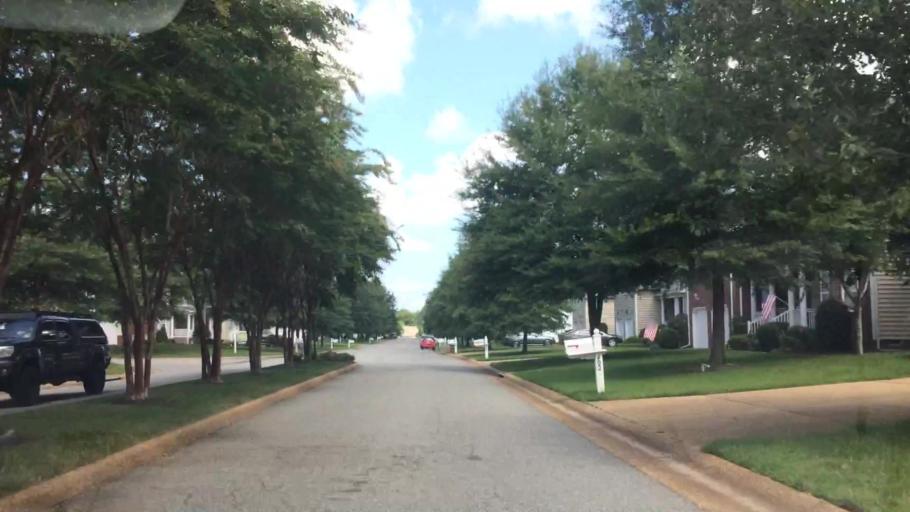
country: US
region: Virginia
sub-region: City of Williamsburg
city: Williamsburg
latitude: 37.2868
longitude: -76.6740
